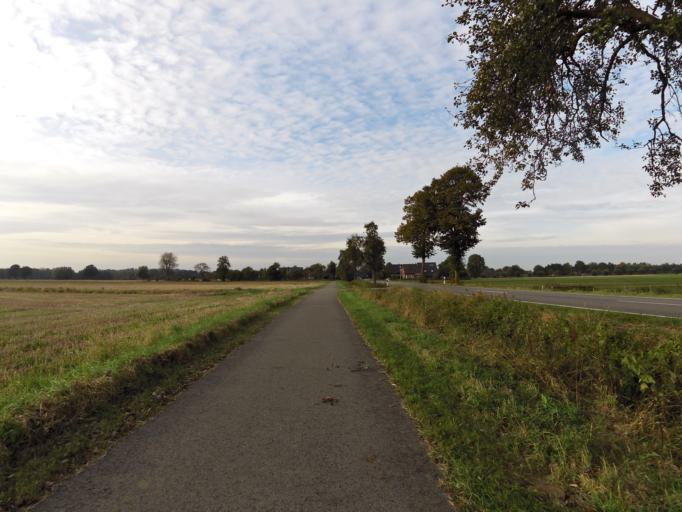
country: DE
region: North Rhine-Westphalia
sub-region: Regierungsbezirk Munster
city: Isselburg
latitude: 51.8072
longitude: 6.5037
